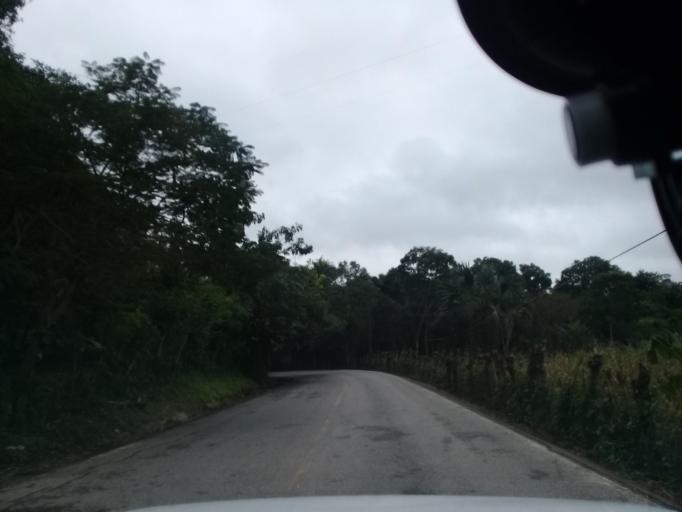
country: MX
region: Veracruz
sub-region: Chalma
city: San Pedro Coyutla
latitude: 21.2179
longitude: -98.4299
